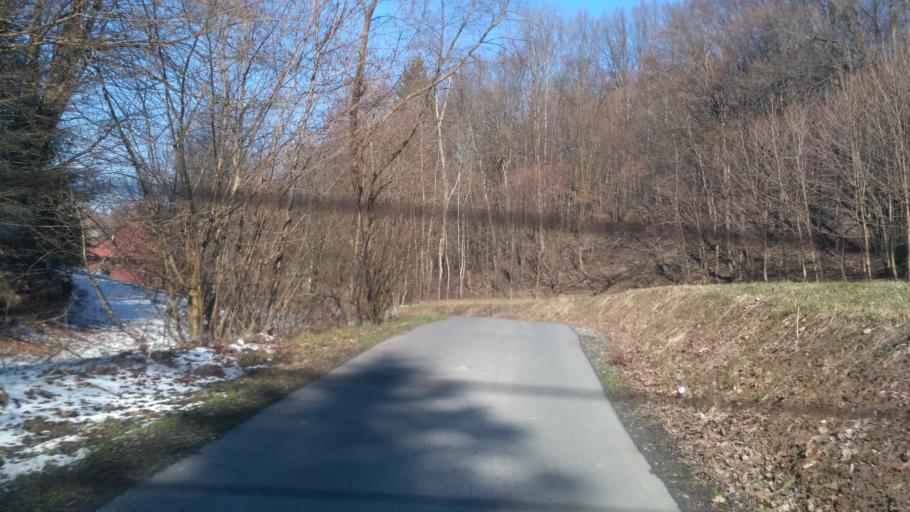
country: PL
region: Subcarpathian Voivodeship
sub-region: Powiat strzyzowski
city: Gwoznica Gorna
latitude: 49.8258
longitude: 22.0031
